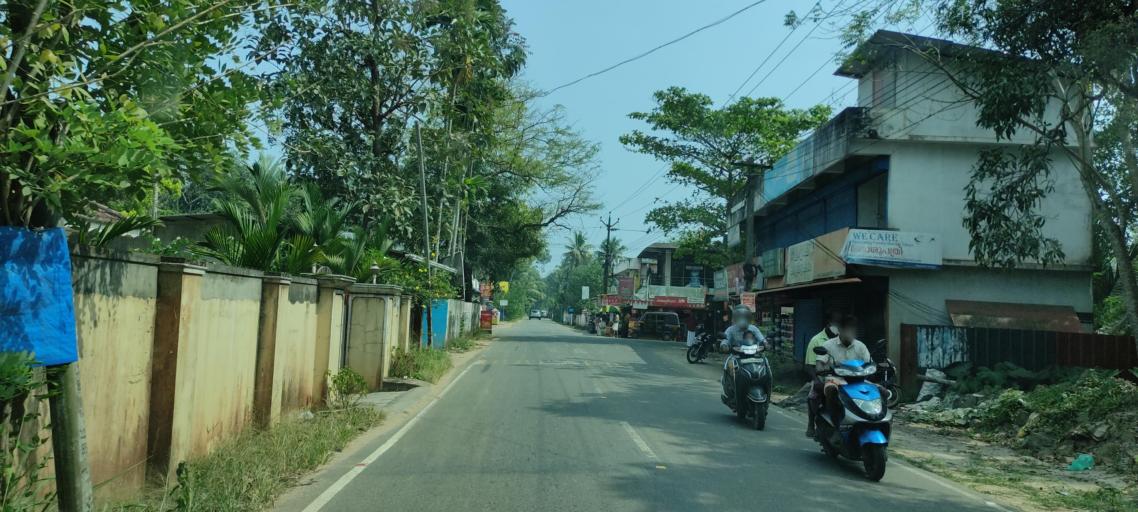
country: IN
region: Kerala
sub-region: Alappuzha
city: Shertallai
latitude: 9.6565
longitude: 76.3582
